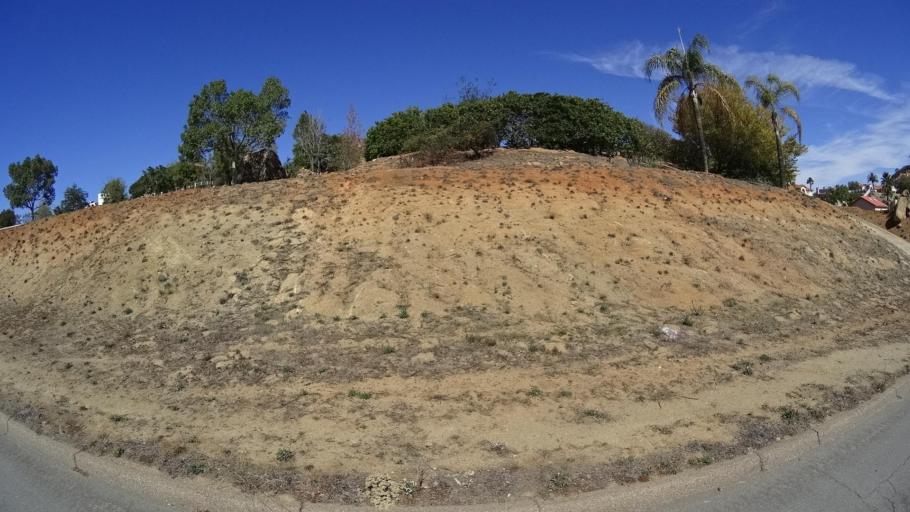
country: US
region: California
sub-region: San Diego County
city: Harbison Canyon
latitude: 32.8778
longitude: -116.8305
